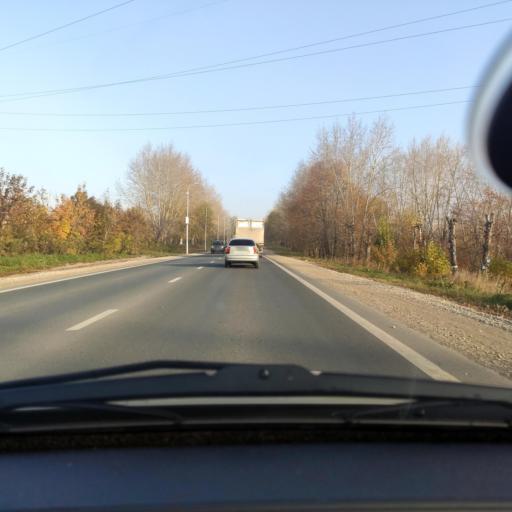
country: RU
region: Bashkortostan
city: Ufa
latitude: 54.8516
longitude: 56.1172
